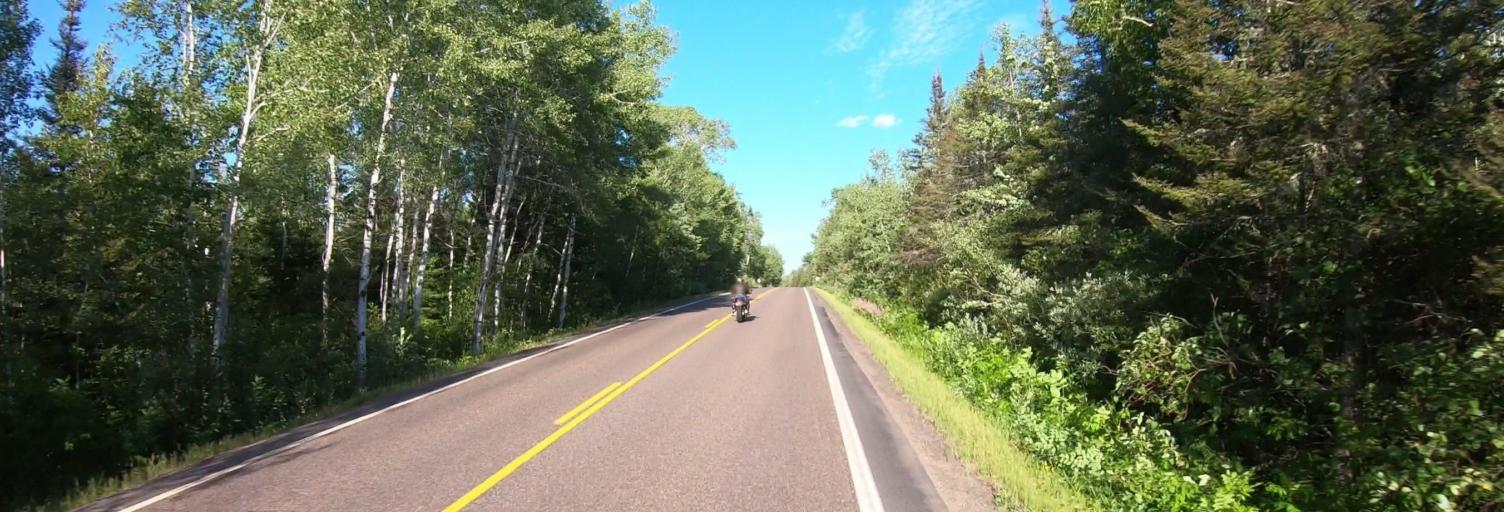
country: US
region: Minnesota
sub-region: Saint Louis County
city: Ely
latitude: 47.9580
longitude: -91.6066
